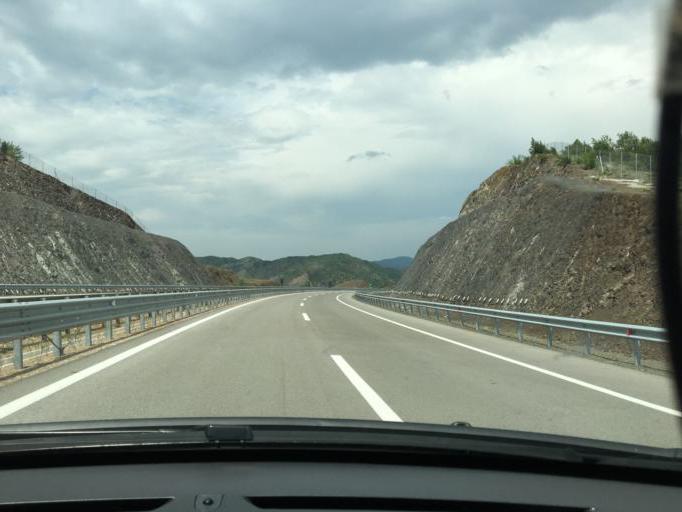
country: MK
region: Gevgelija
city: Miravci
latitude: 41.3606
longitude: 22.3478
